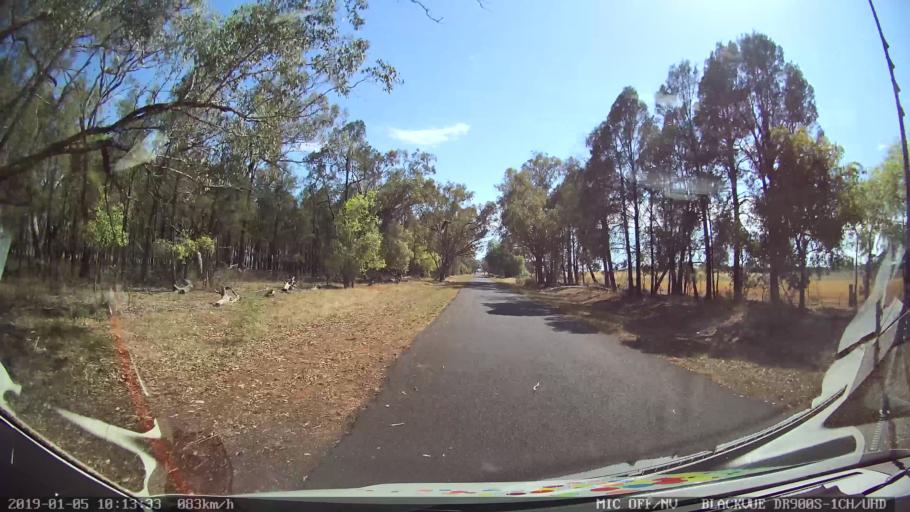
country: AU
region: New South Wales
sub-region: Gilgandra
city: Gilgandra
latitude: -31.6011
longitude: 148.9260
